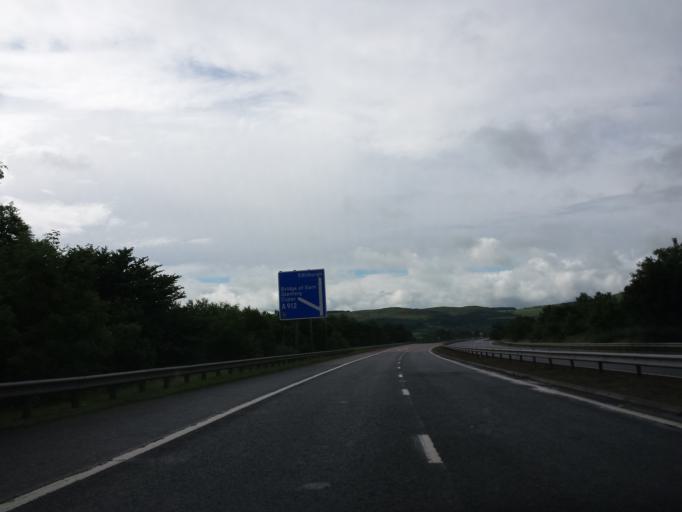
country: GB
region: Scotland
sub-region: Perth and Kinross
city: Bridge of Earn
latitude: 56.3485
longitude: -3.3968
